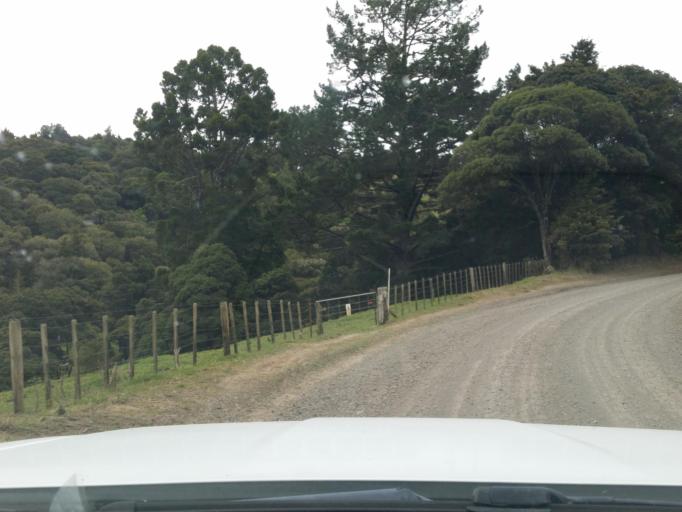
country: NZ
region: Northland
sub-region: Kaipara District
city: Dargaville
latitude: -35.7123
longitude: 173.6324
